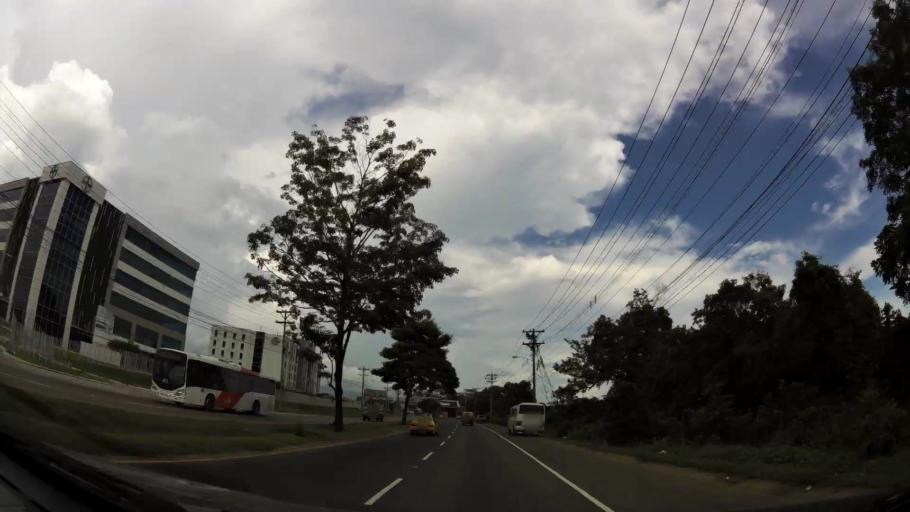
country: PA
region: Panama
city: Tocumen
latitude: 9.0697
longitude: -79.3952
